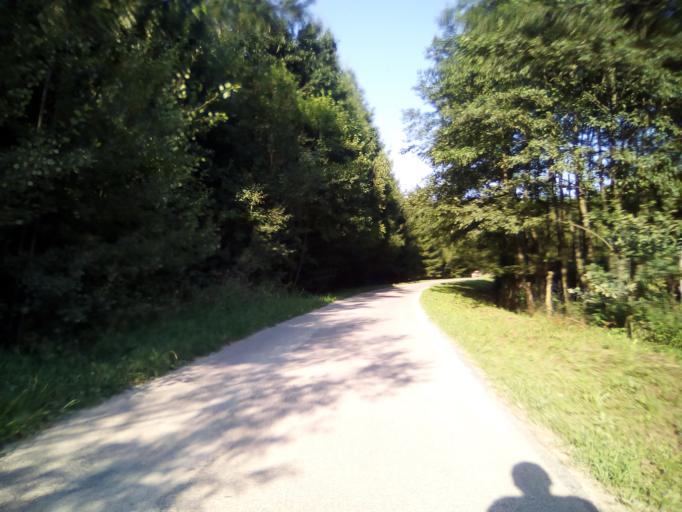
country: PL
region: Subcarpathian Voivodeship
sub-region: Powiat brzozowski
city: Domaradz
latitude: 49.8153
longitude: 21.9490
